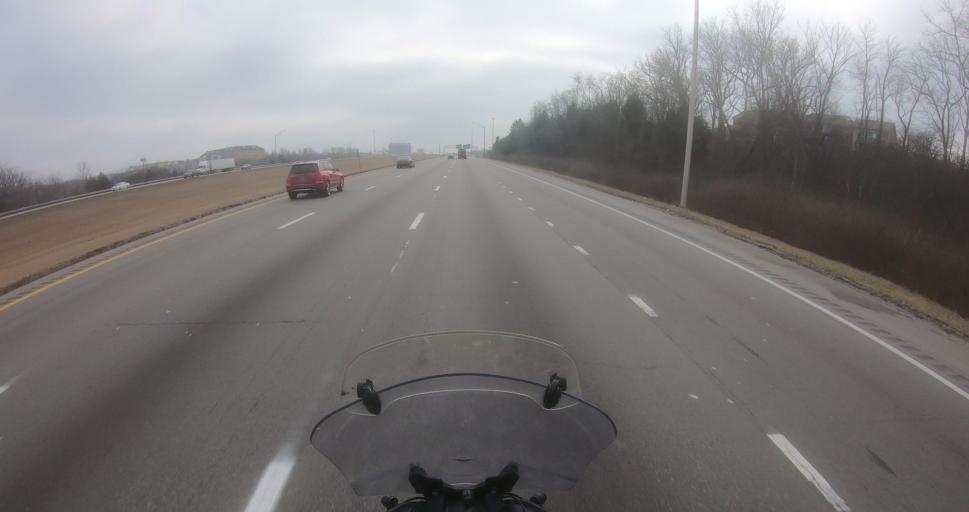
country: US
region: Ohio
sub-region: Montgomery County
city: West Carrollton City
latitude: 39.6475
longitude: -84.2337
